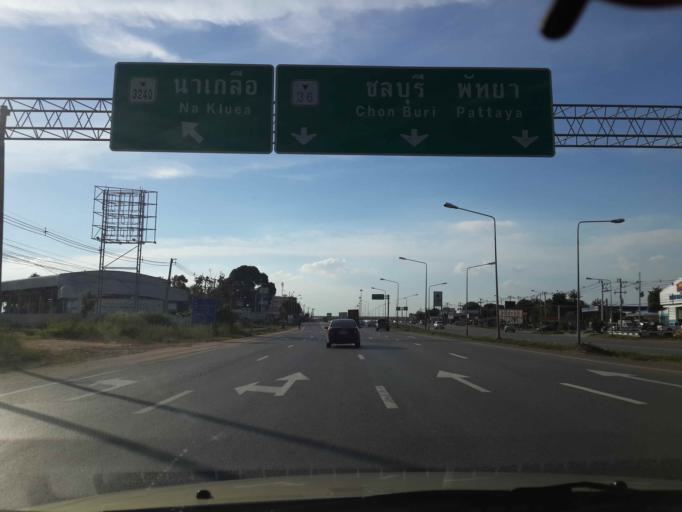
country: TH
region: Chon Buri
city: Phatthaya
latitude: 12.9480
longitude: 100.9908
